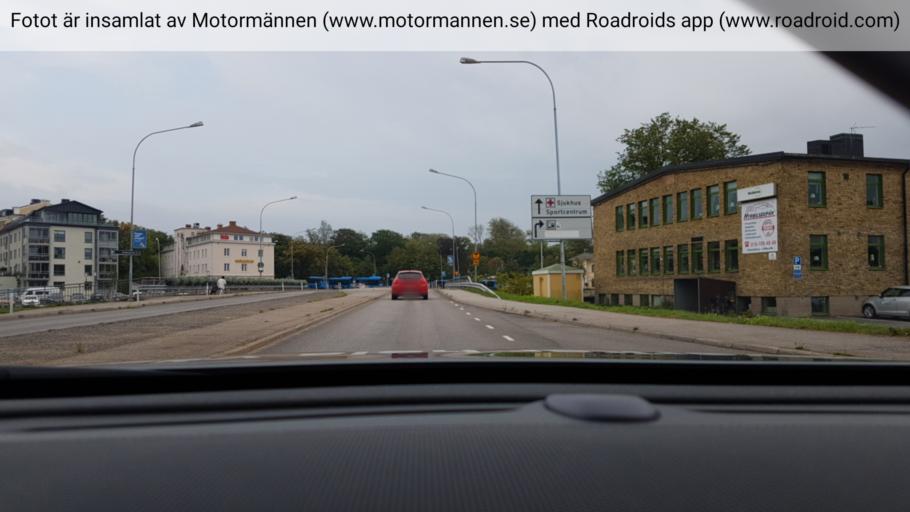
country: SE
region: Vaestra Goetaland
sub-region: Vanersborgs Kommun
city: Vanersborg
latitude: 58.3796
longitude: 12.3170
